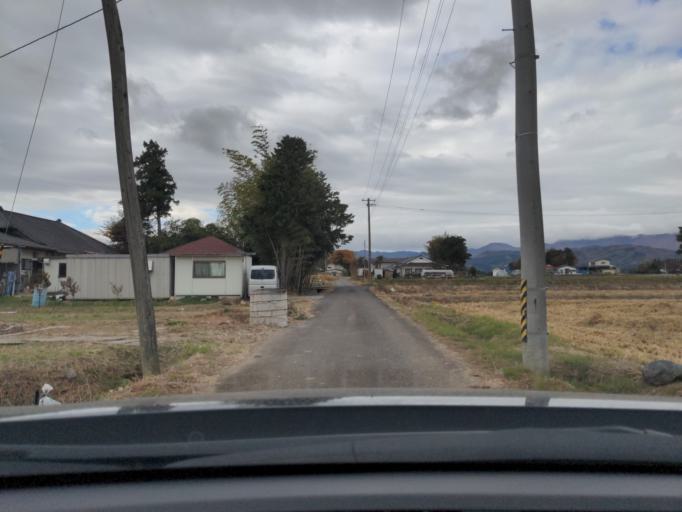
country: JP
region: Fukushima
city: Koriyama
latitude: 37.4081
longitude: 140.3043
